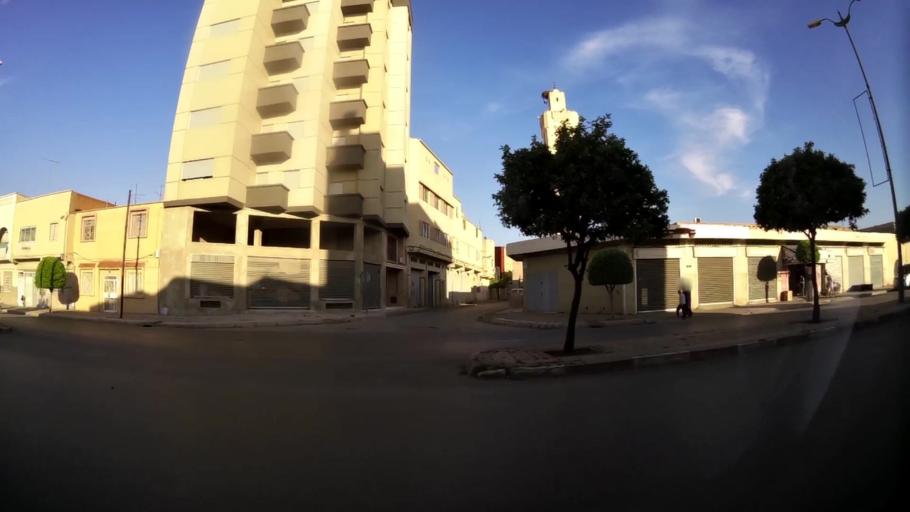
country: MA
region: Oriental
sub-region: Oujda-Angad
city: Oujda
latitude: 34.6939
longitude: -1.9057
